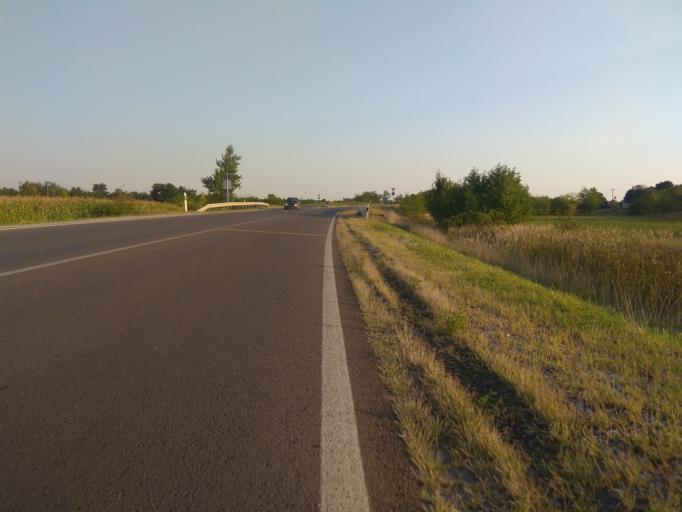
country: HU
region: Borsod-Abauj-Zemplen
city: Emod
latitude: 47.9433
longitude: 20.8307
